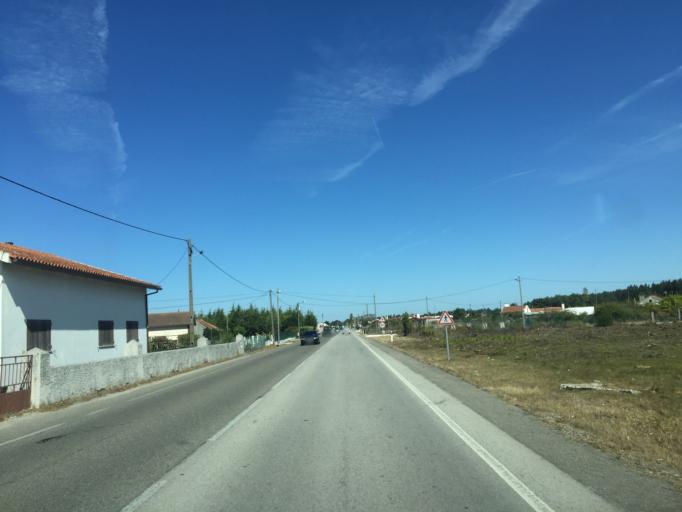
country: PT
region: Coimbra
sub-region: Figueira da Foz
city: Alhadas
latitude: 40.2279
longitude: -8.8021
